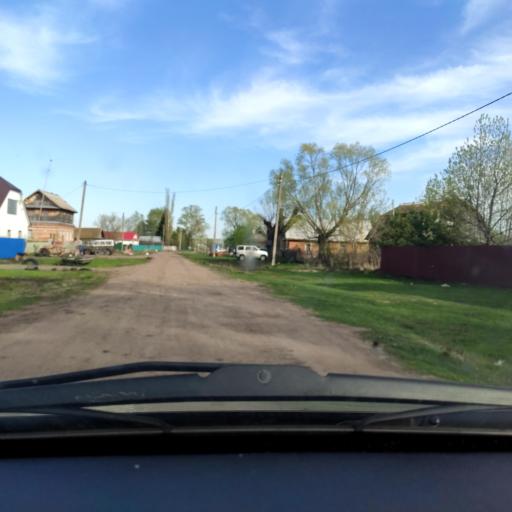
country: RU
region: Bashkortostan
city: Asanovo
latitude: 55.0007
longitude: 55.4914
